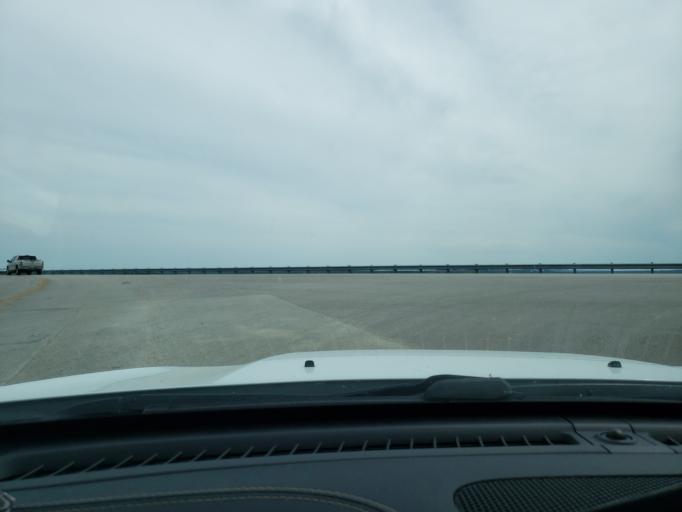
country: US
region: Texas
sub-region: Burleson County
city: Somerville
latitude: 30.3354
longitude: -96.5392
